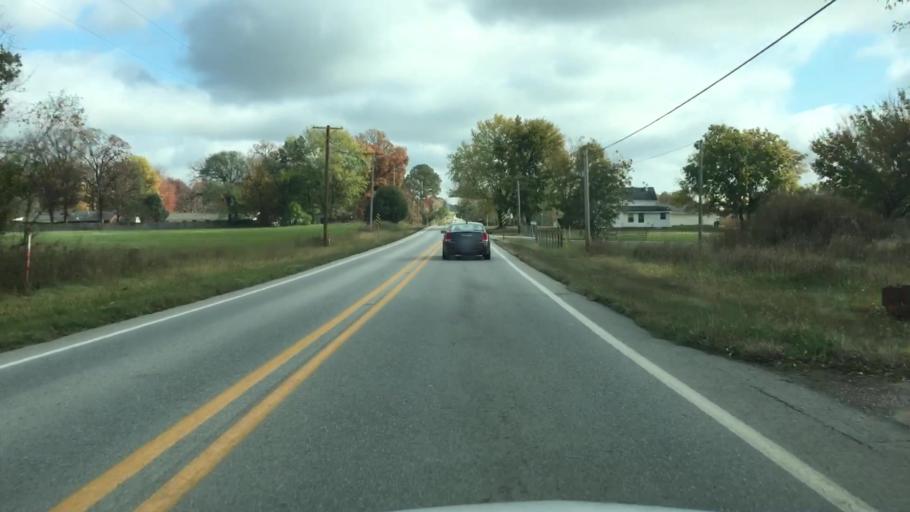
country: US
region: Arkansas
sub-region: Benton County
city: Gentry
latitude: 36.2638
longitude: -94.4768
